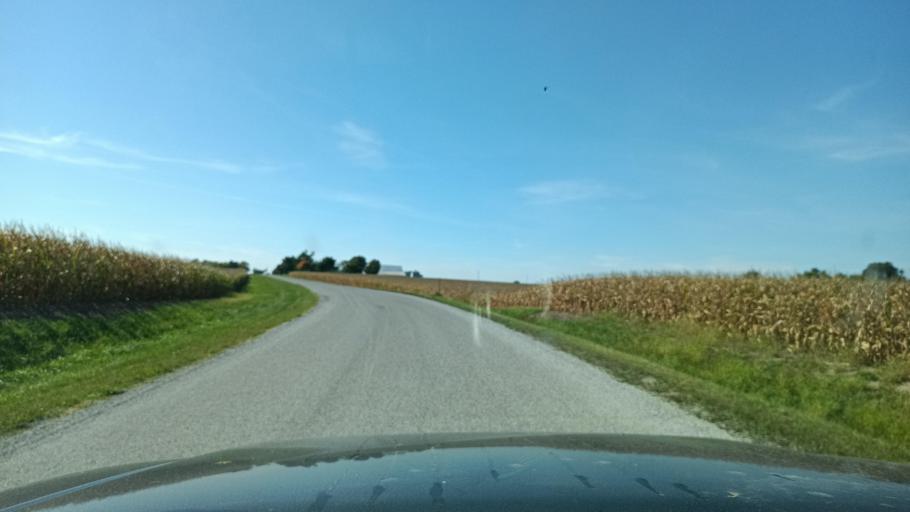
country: US
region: Illinois
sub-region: Logan County
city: Atlanta
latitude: 40.2436
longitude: -89.1865
